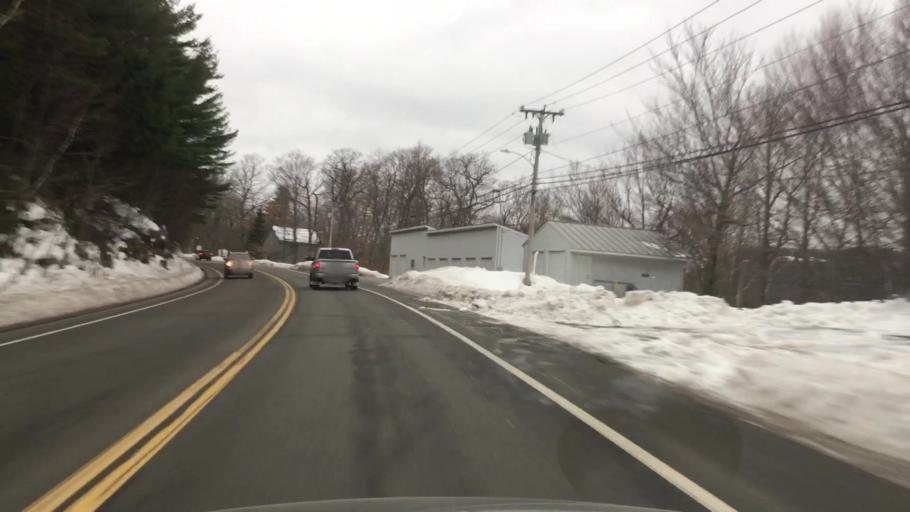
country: US
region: New Hampshire
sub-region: Merrimack County
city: Newbury
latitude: 43.3404
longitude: -72.0592
